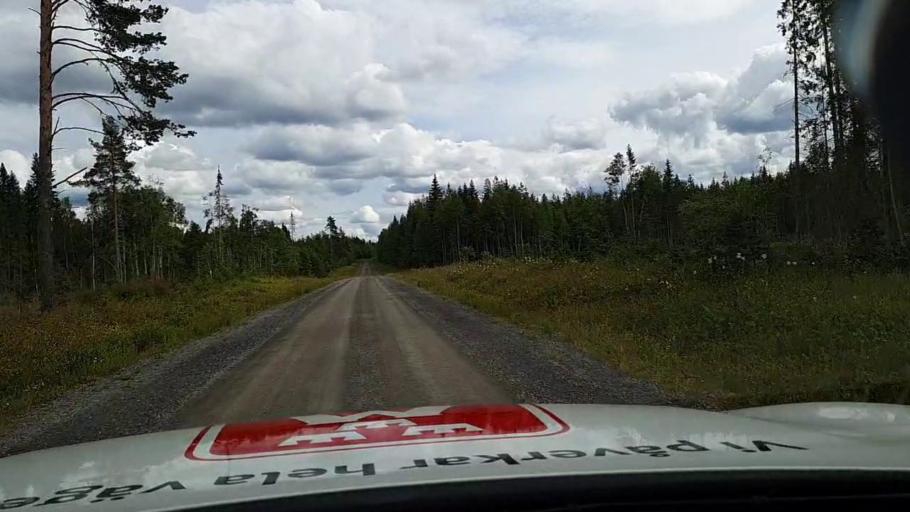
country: SE
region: Jaemtland
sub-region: OEstersunds Kommun
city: Lit
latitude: 63.3069
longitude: 15.2628
